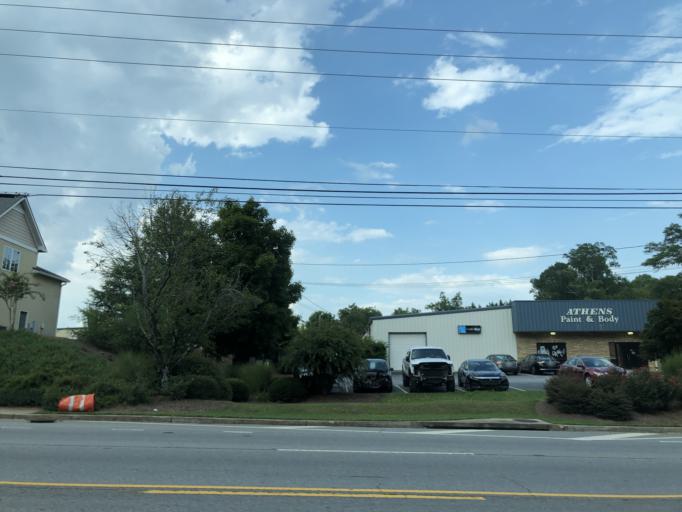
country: US
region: Georgia
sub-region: Clarke County
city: Athens
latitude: 33.9445
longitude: -83.3367
